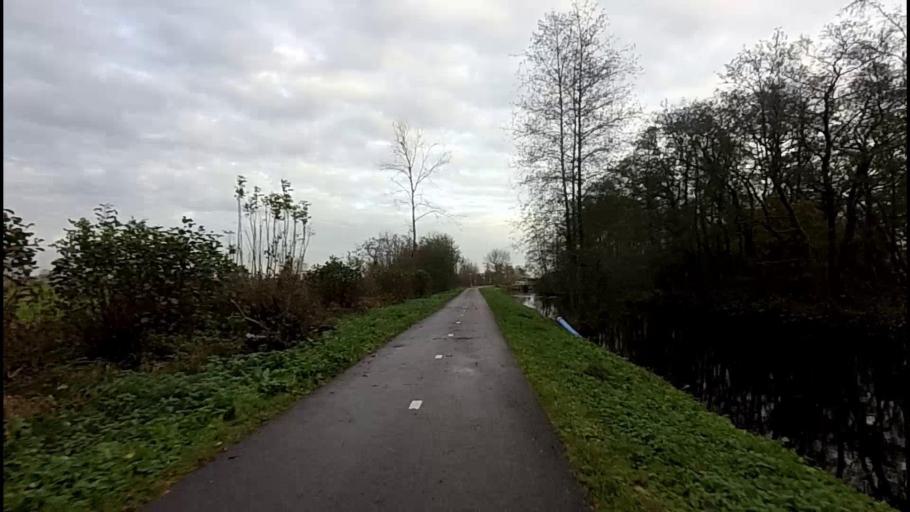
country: NL
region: South Holland
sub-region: Molenwaard
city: Nieuw-Lekkerland
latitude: 51.9300
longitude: 4.7144
